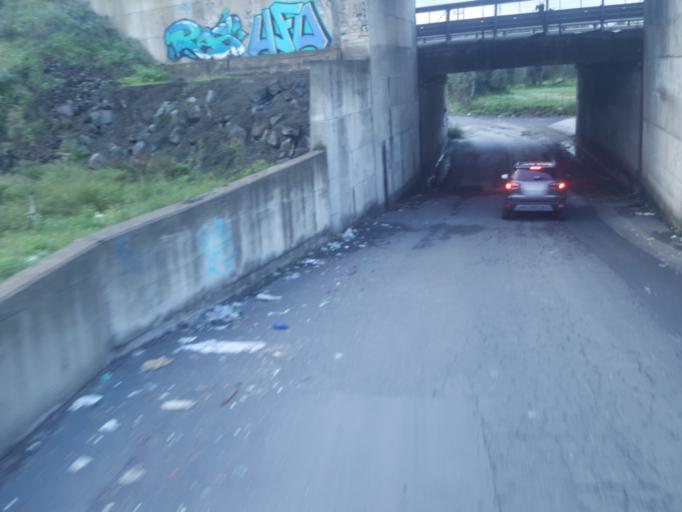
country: IT
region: Sicily
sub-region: Catania
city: Belvedere-Piano Tavola
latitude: 37.5389
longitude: 14.9672
